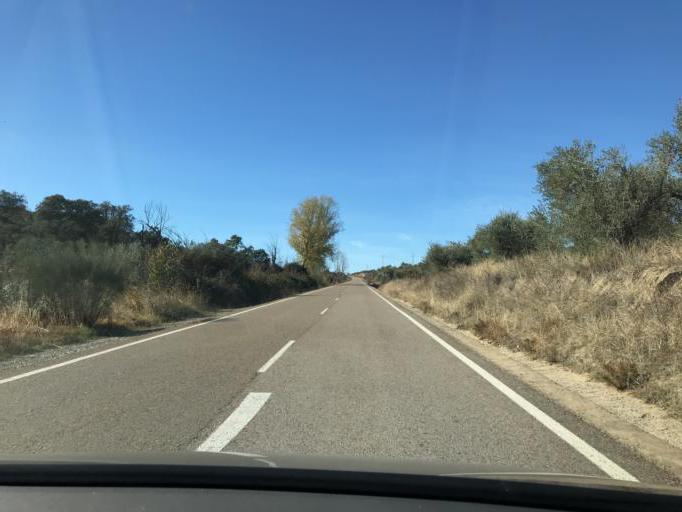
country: ES
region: Extremadura
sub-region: Provincia de Badajoz
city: Valverde de Llerena
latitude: 38.2415
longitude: -5.7901
